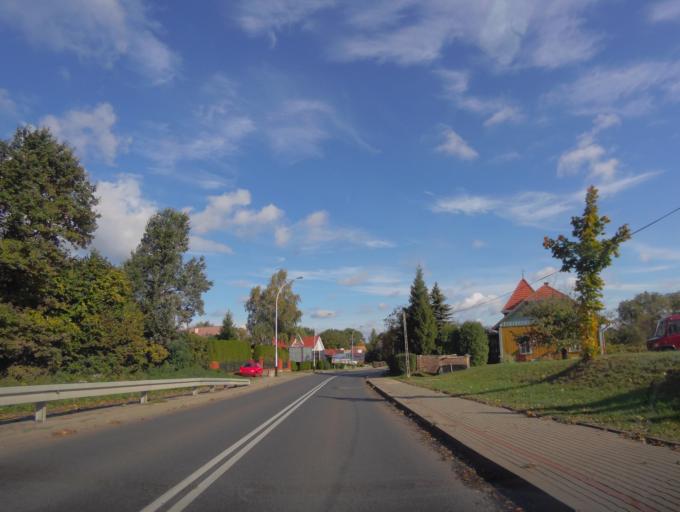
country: PL
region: Subcarpathian Voivodeship
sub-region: Powiat lezajski
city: Lezajsk
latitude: 50.2480
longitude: 22.4135
